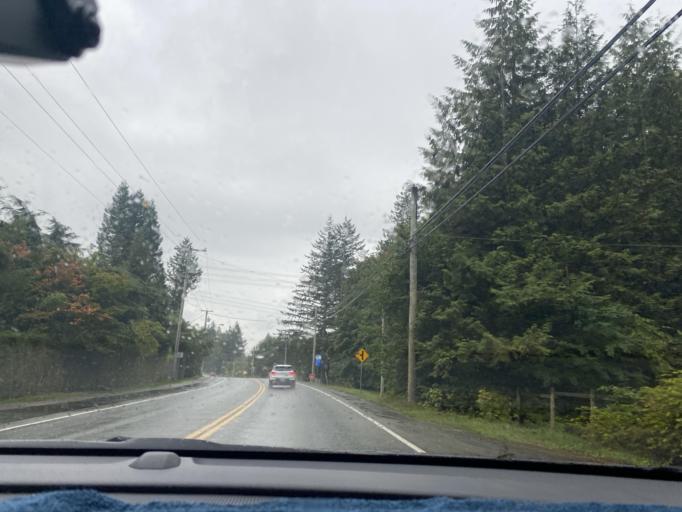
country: CA
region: British Columbia
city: Agassiz
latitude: 49.2819
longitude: -121.7828
